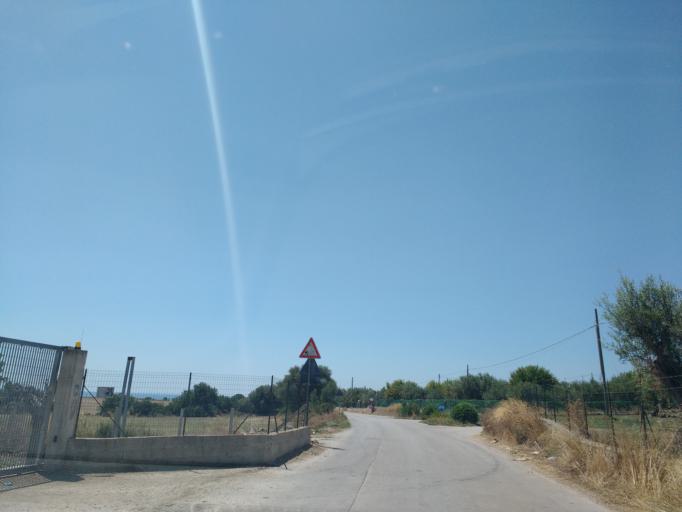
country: IT
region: Sicily
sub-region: Ragusa
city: Pozzallo
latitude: 36.7379
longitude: 14.8929
